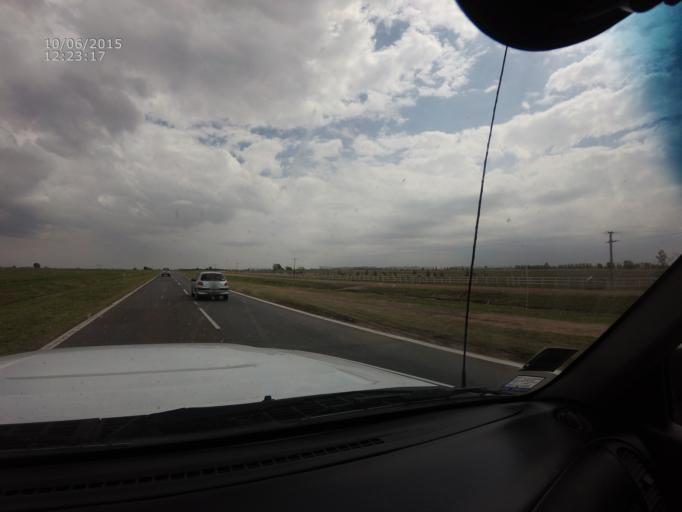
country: AR
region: Santa Fe
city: Roldan
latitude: -32.9147
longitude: -60.9541
